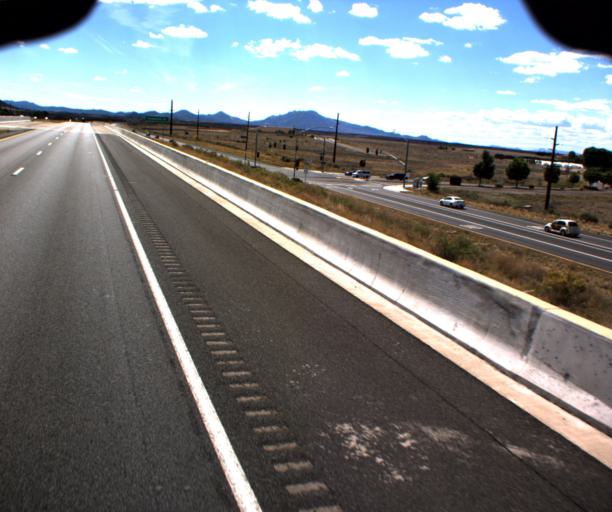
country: US
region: Arizona
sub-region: Yavapai County
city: Prescott Valley
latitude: 34.6372
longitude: -112.3324
